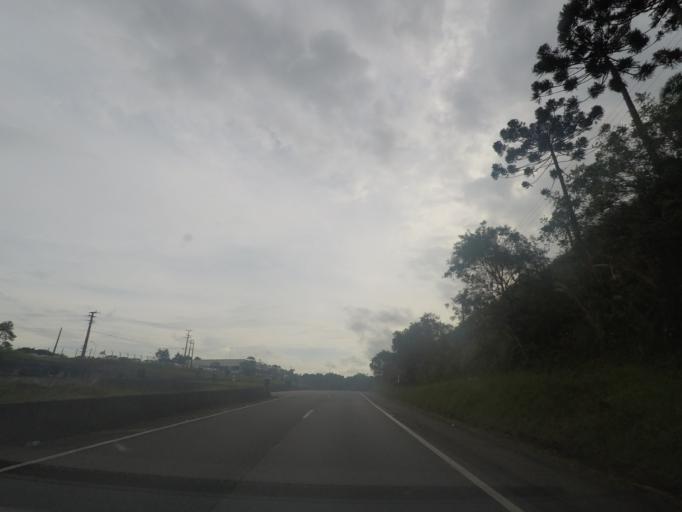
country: BR
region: Parana
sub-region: Quatro Barras
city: Quatro Barras
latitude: -25.3464
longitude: -49.0462
